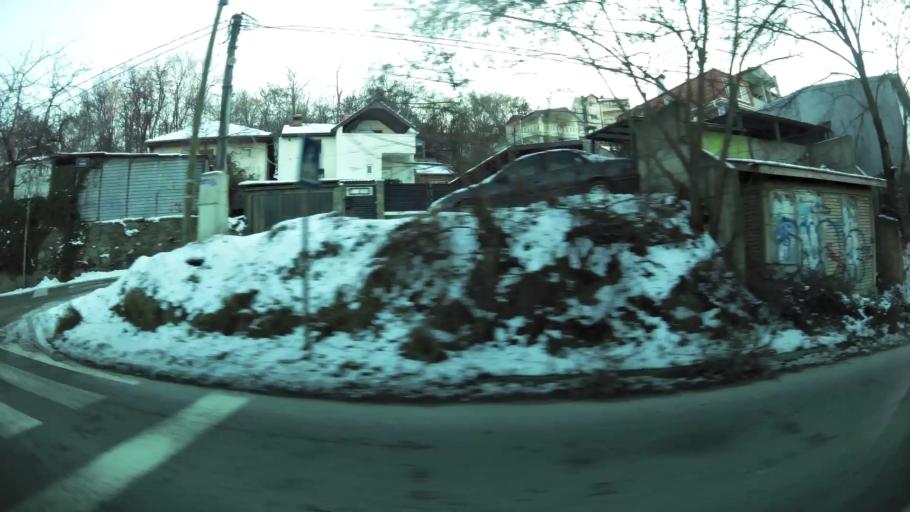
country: MK
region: Karpos
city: Skopje
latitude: 41.9958
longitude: 21.3925
